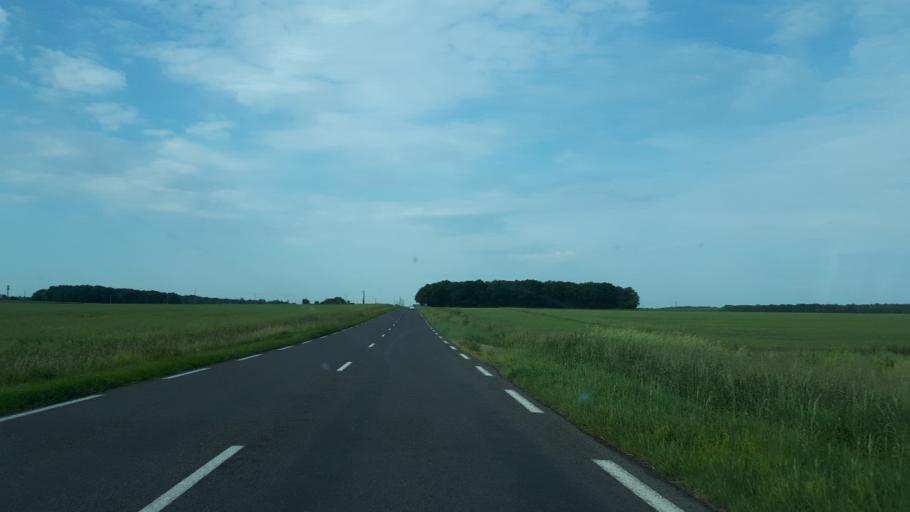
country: FR
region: Centre
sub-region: Departement d'Indre-et-Loire
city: Monnaie
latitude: 47.5270
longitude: 0.8311
